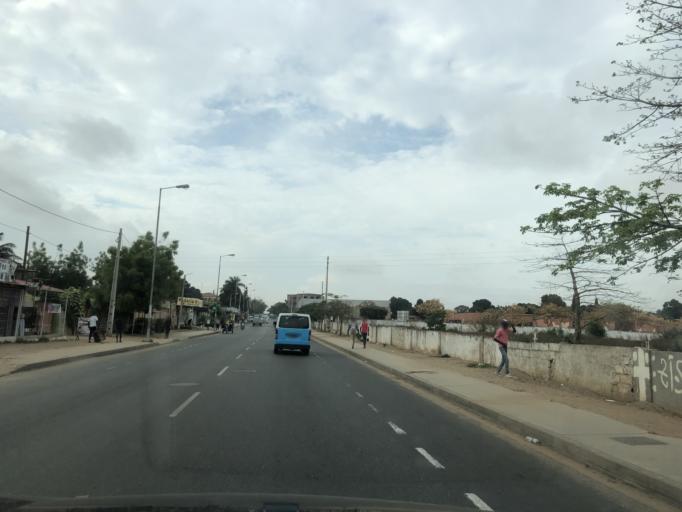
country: AO
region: Luanda
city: Luanda
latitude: -8.9153
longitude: 13.3739
